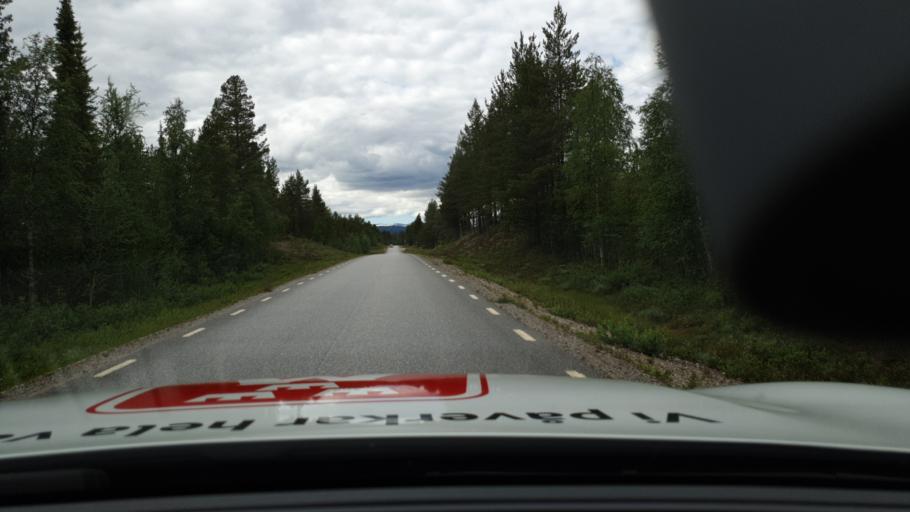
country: SE
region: Norrbotten
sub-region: Arjeplogs Kommun
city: Arjeplog
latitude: 66.8848
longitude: 18.0601
